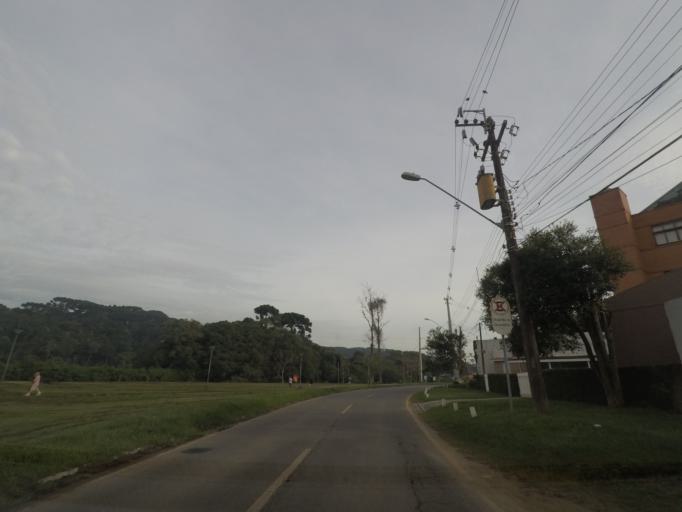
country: BR
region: Parana
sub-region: Curitiba
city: Curitiba
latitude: -25.4258
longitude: -49.3061
